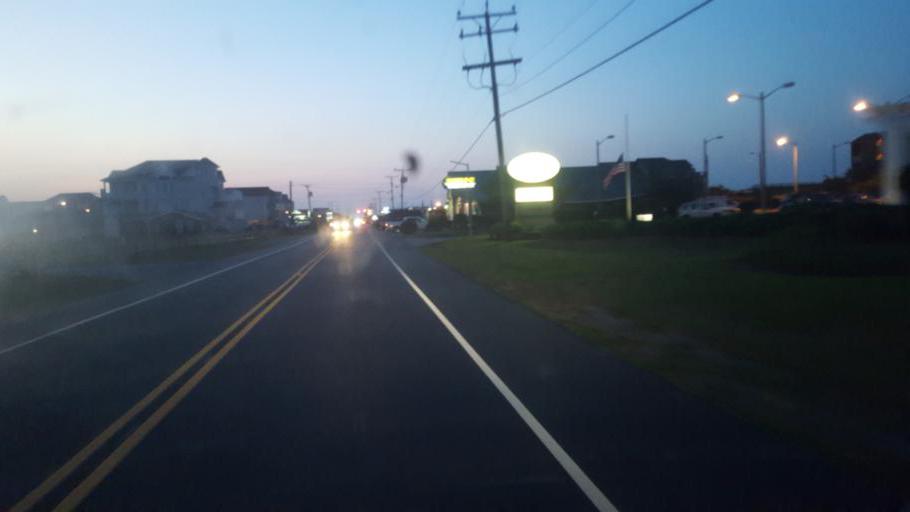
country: US
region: North Carolina
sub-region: Dare County
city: Kill Devil Hills
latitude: 36.0121
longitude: -75.6562
